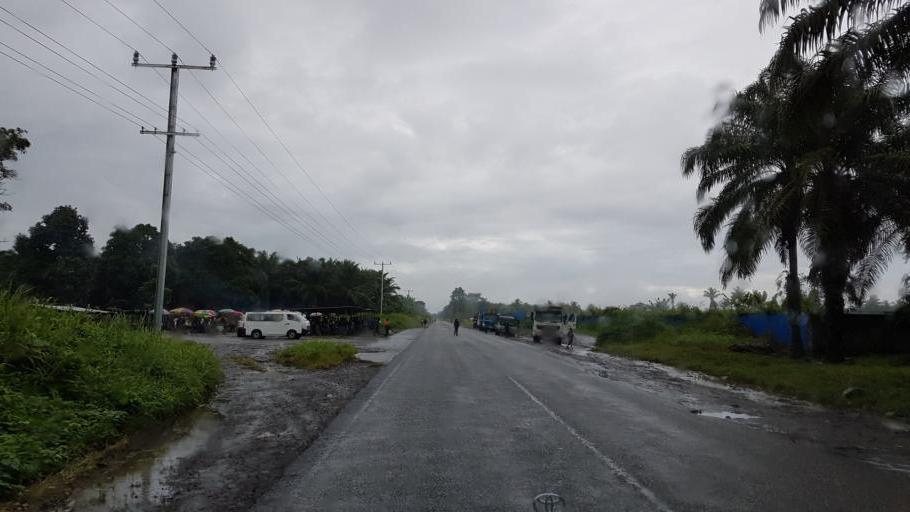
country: PG
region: Northern Province
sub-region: Sohe
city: Popondetta
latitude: -8.7489
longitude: 148.2053
